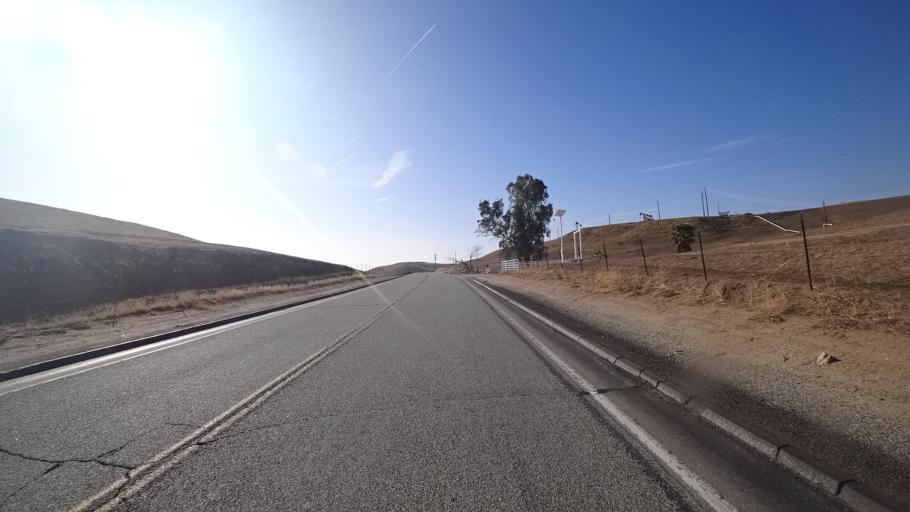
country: US
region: California
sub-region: Kern County
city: Oildale
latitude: 35.4966
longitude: -118.9958
